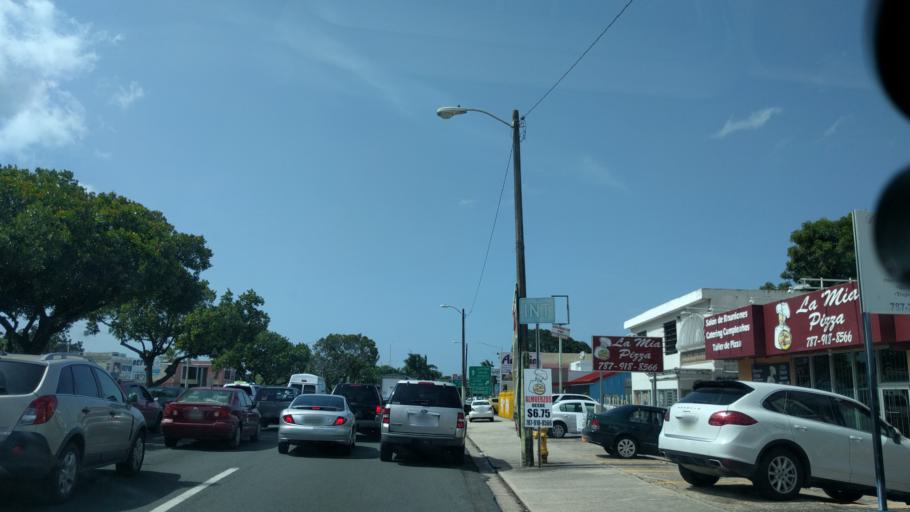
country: PR
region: Bayamon
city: Bayamon
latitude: 18.4186
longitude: -66.1636
